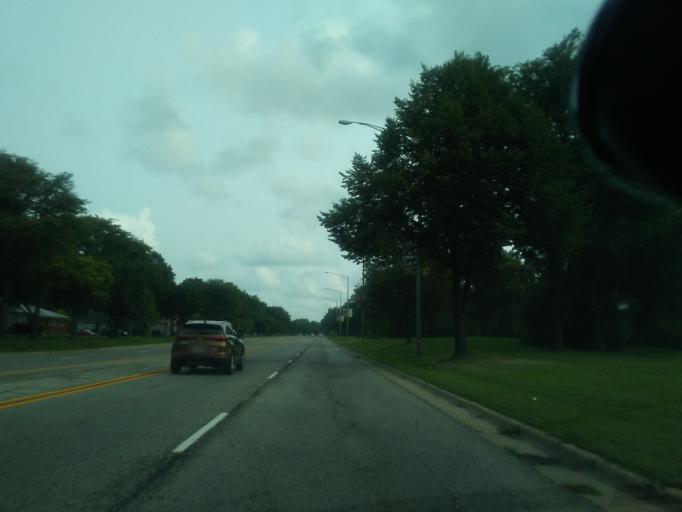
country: US
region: Illinois
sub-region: Cook County
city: Evanston
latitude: 42.0435
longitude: -87.7106
